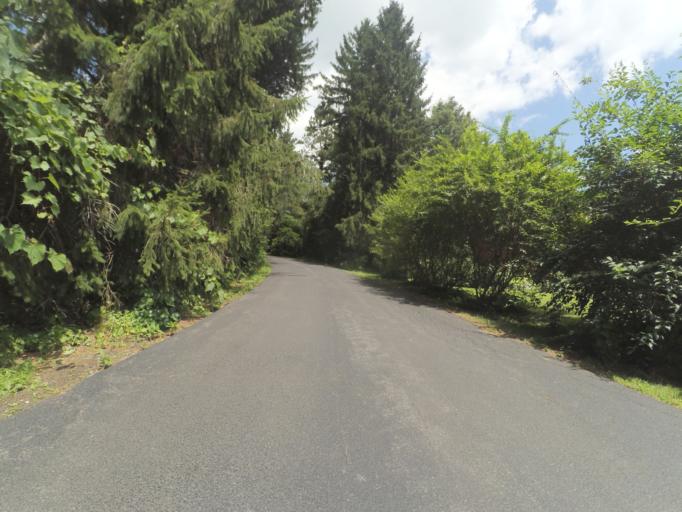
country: US
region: Pennsylvania
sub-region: Centre County
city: Boalsburg
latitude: 40.7836
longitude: -77.8014
